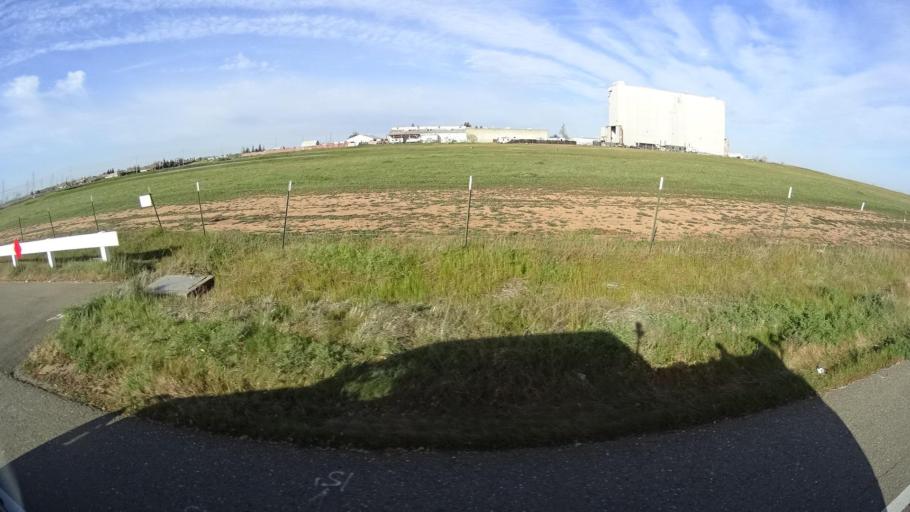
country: US
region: California
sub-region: Sacramento County
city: Gold River
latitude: 38.5635
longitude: -121.2069
